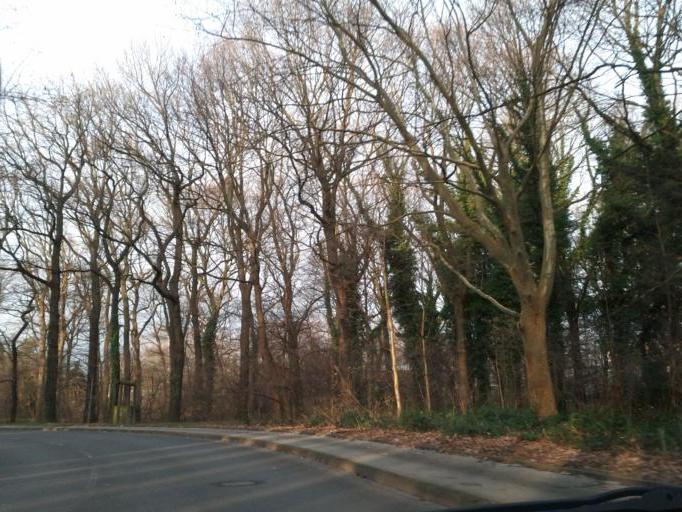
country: DE
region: North Rhine-Westphalia
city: Lanstrop
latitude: 51.5482
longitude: 7.5371
